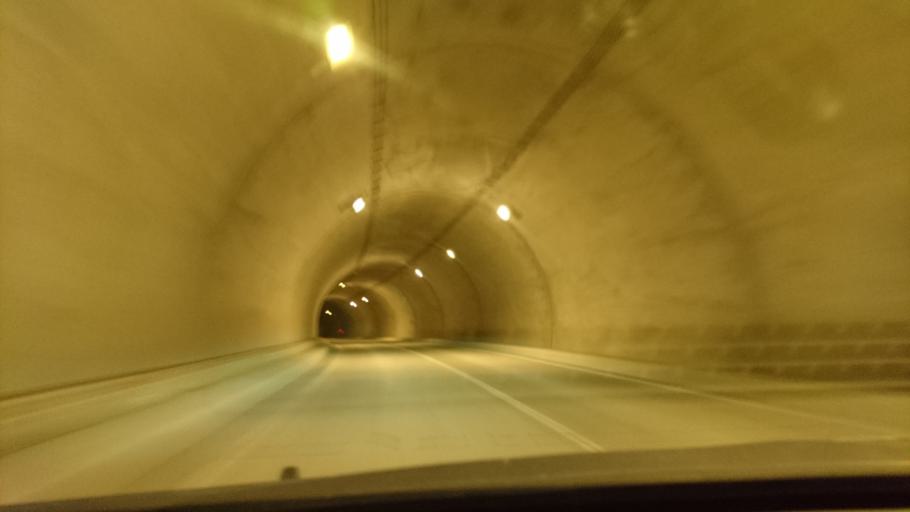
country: JP
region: Akita
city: Yuzawa
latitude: 39.0397
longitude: 140.7344
